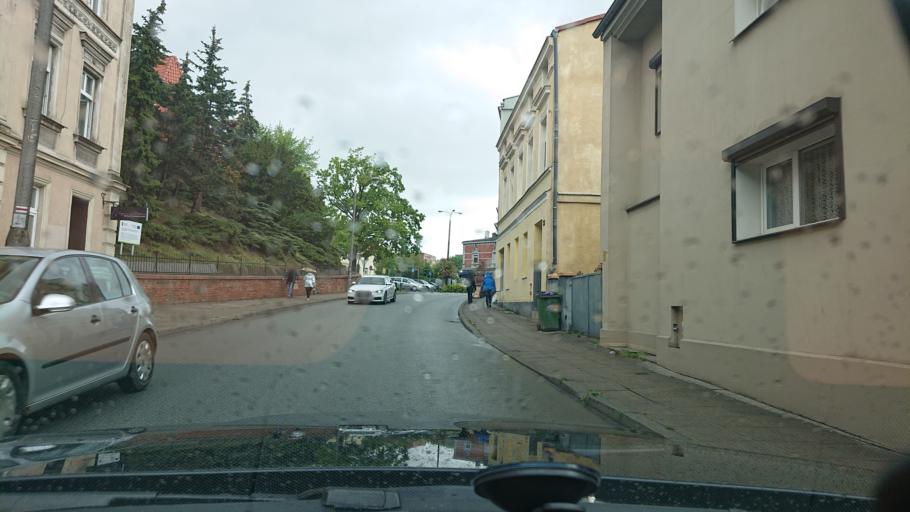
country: PL
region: Greater Poland Voivodeship
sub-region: Powiat gnieznienski
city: Gniezno
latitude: 52.5375
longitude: 17.5983
